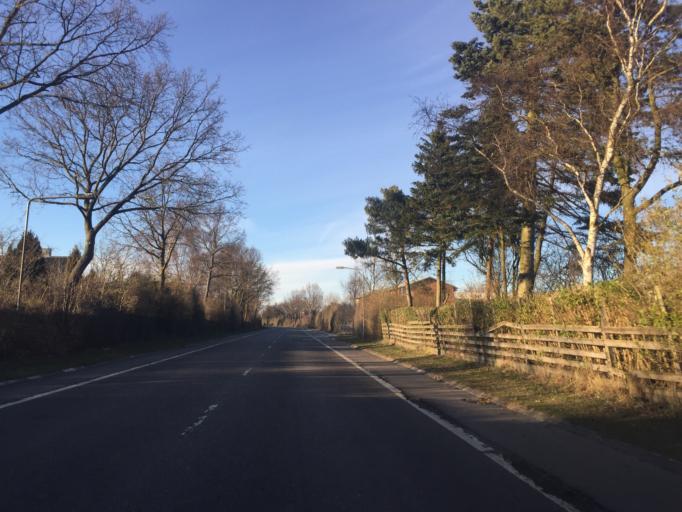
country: DK
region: Capital Region
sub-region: Dragor Kommune
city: Dragor
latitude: 55.5904
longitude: 12.6572
